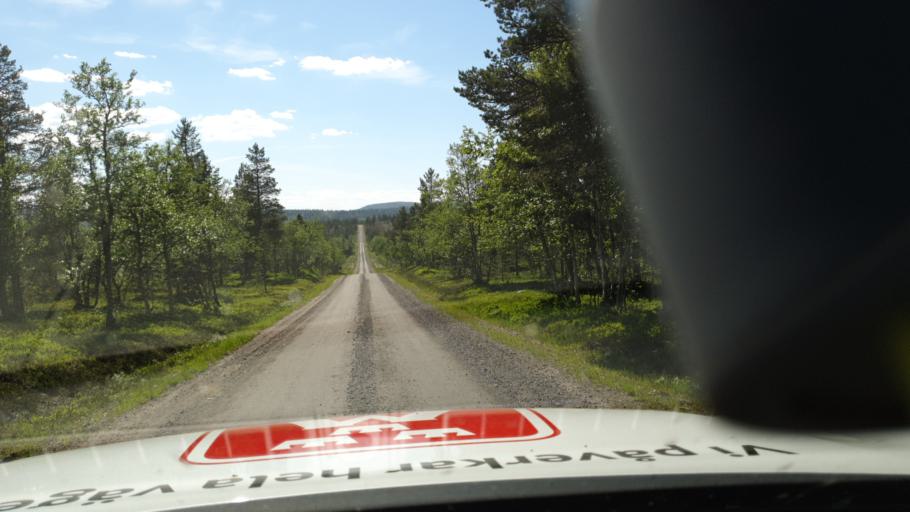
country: NO
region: Hedmark
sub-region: Engerdal
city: Engerdal
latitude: 62.1380
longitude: 12.9347
